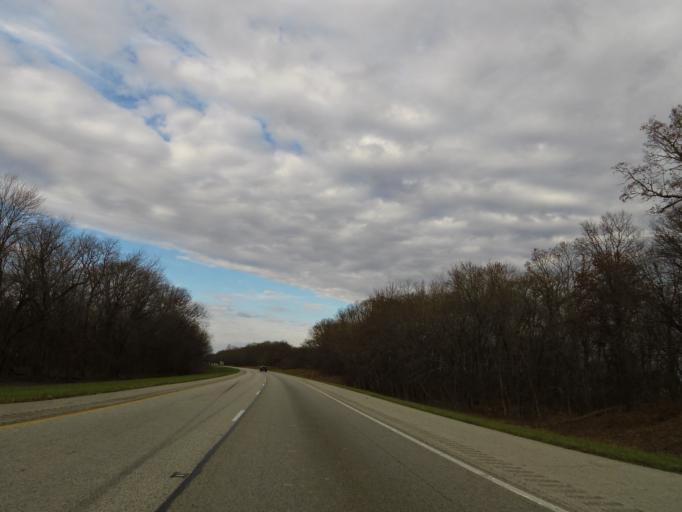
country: US
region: Illinois
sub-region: Washington County
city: Nashville
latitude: 38.4075
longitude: -89.4103
